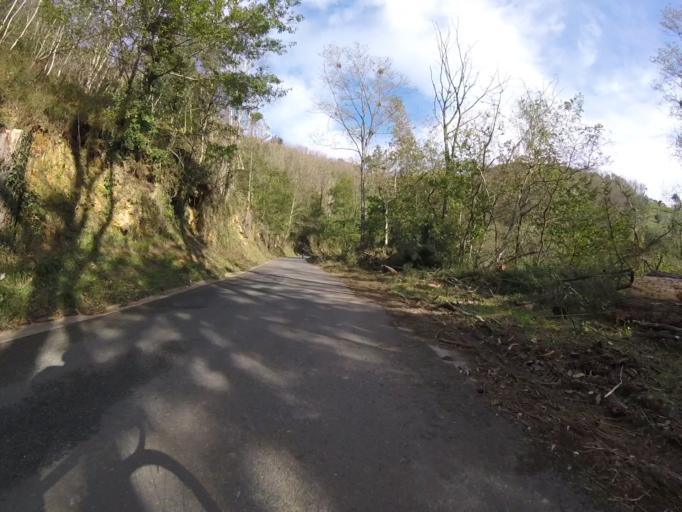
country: ES
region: Basque Country
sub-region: Provincia de Guipuzcoa
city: Orio
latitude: 43.2873
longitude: -2.1032
